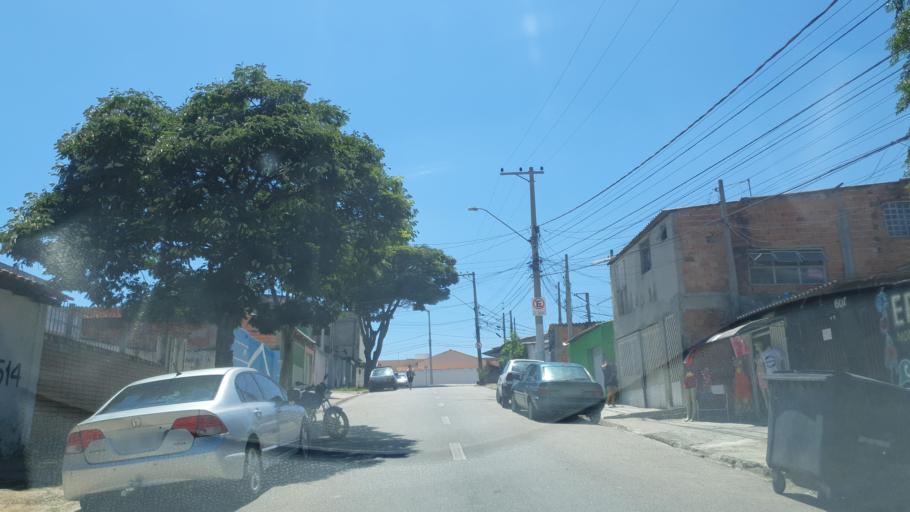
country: BR
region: Sao Paulo
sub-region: Sorocaba
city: Sorocaba
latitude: -23.4725
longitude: -47.5063
